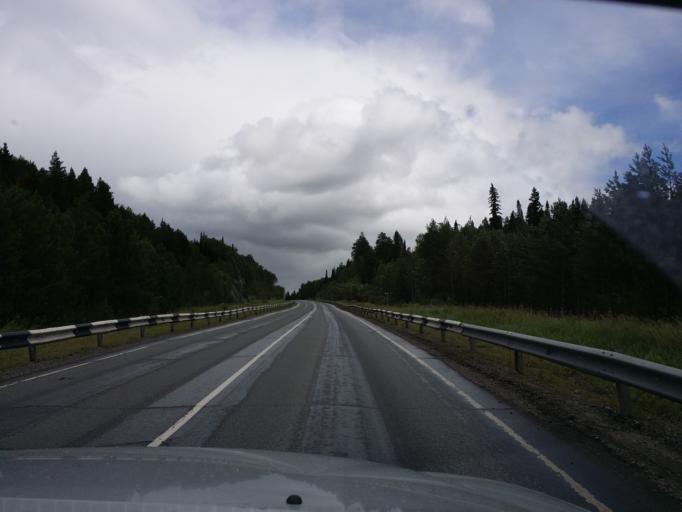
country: RU
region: Tjumen
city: Abalak
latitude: 58.4684
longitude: 68.5570
